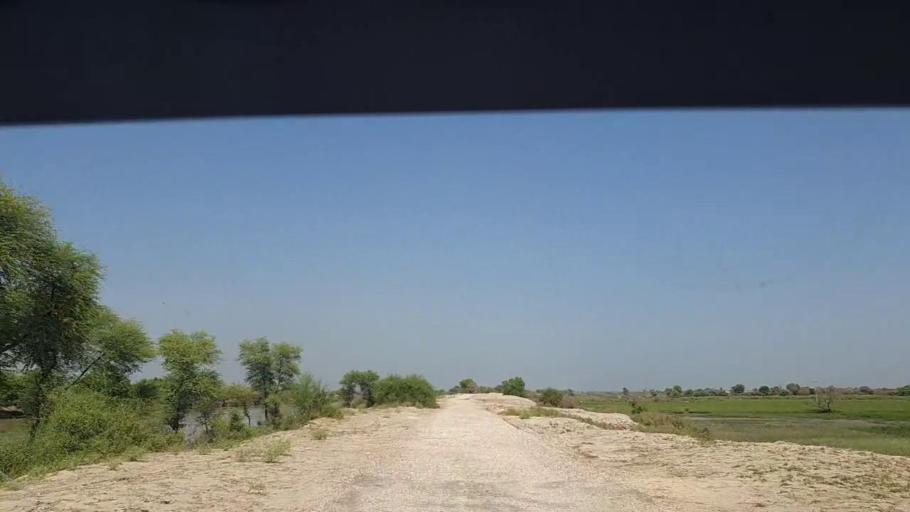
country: PK
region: Sindh
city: Kandhkot
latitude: 28.1910
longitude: 69.1642
